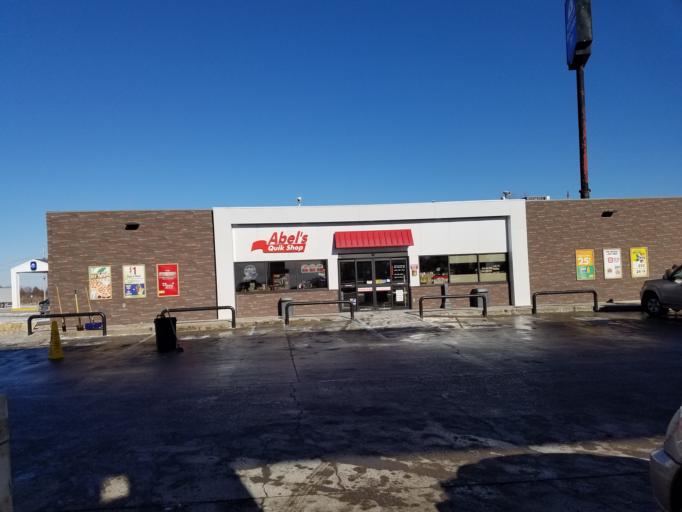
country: US
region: Missouri
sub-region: Montgomery County
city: Montgomery City
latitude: 38.9018
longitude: -91.4588
